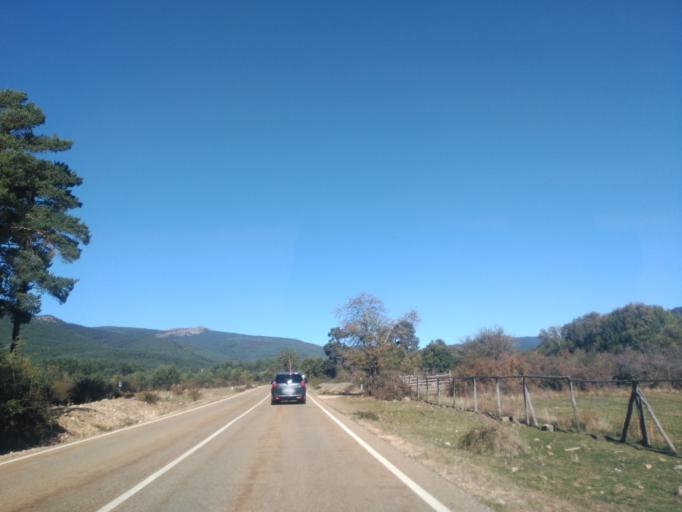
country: ES
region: Castille and Leon
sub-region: Provincia de Soria
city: Vinuesa
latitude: 41.9613
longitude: -2.7779
